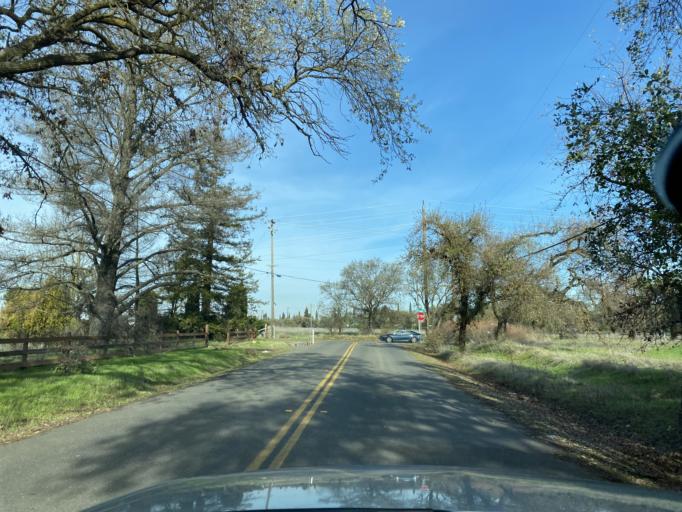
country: US
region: California
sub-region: Sacramento County
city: Elk Grove
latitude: 38.3940
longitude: -121.3809
